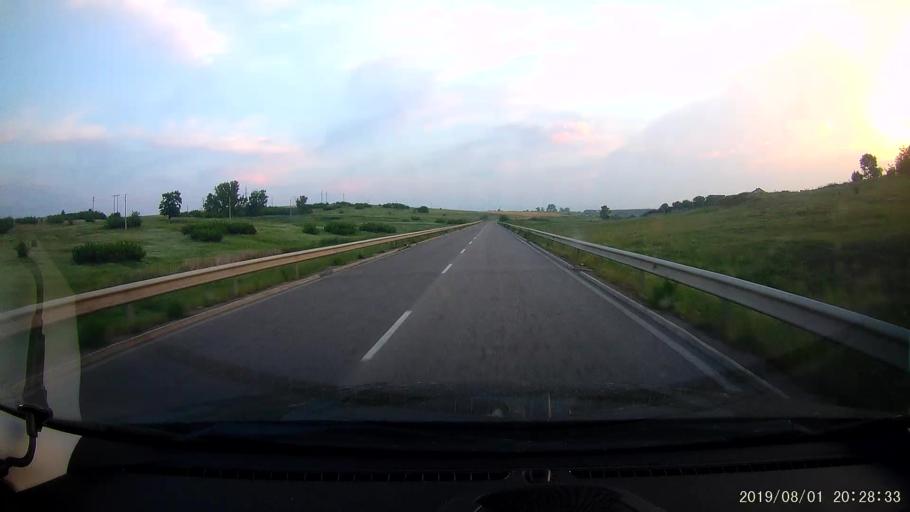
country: BG
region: Yambol
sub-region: Obshtina Elkhovo
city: Elkhovo
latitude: 42.1674
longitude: 26.5758
